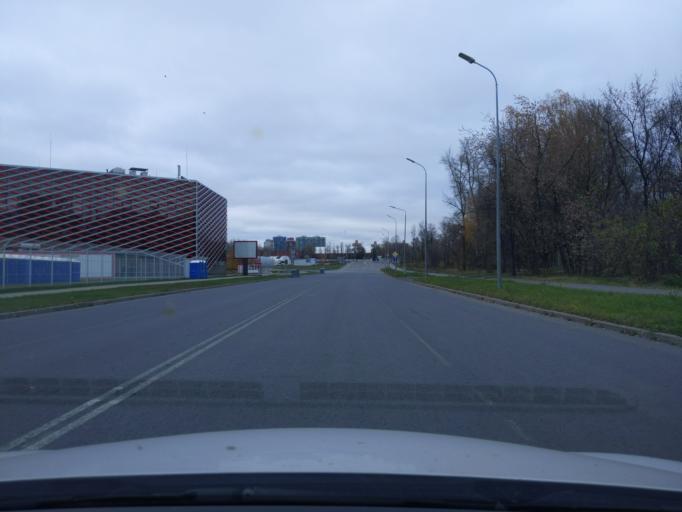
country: RU
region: Moscow
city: Pokrovskoye-Streshnevo
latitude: 55.8171
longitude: 37.4430
